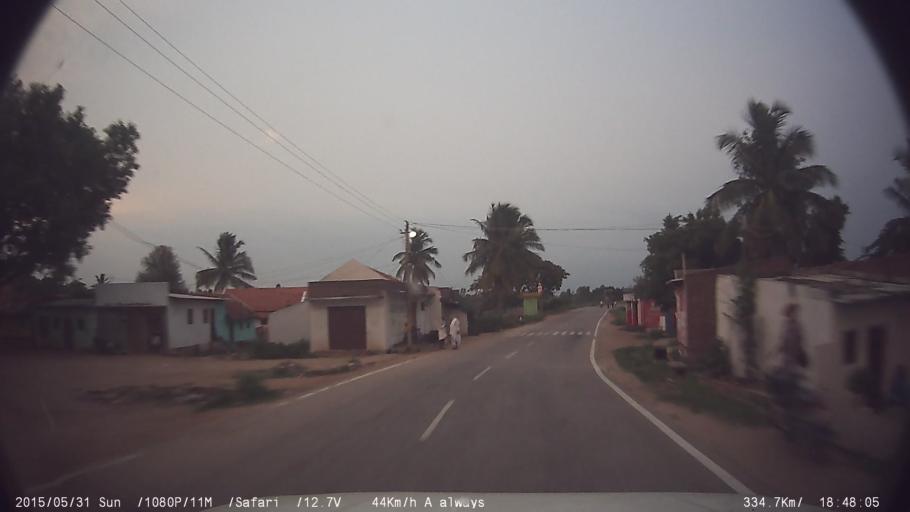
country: IN
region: Karnataka
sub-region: Mysore
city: Tirumakudal Narsipur
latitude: 12.1681
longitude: 76.8412
